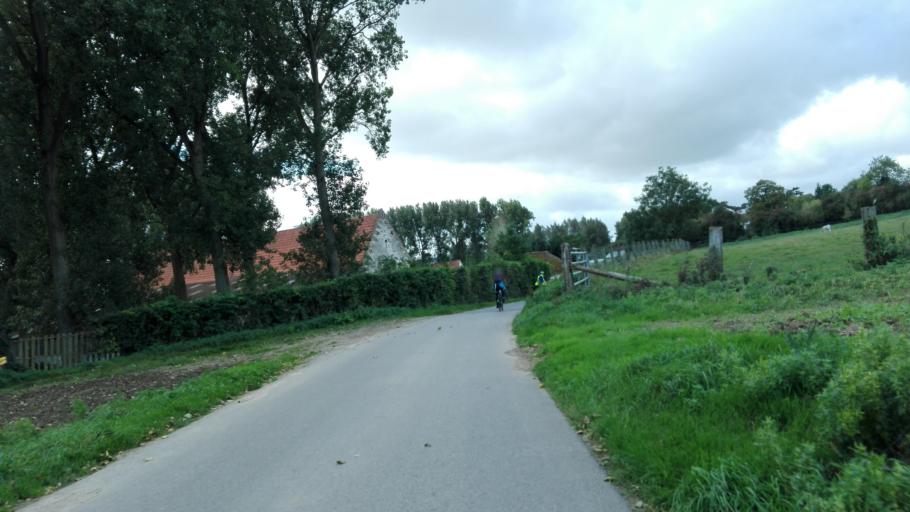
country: FR
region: Nord-Pas-de-Calais
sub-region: Departement du Pas-de-Calais
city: Tournehem-sur-la-Hem
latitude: 50.8039
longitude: 2.0338
